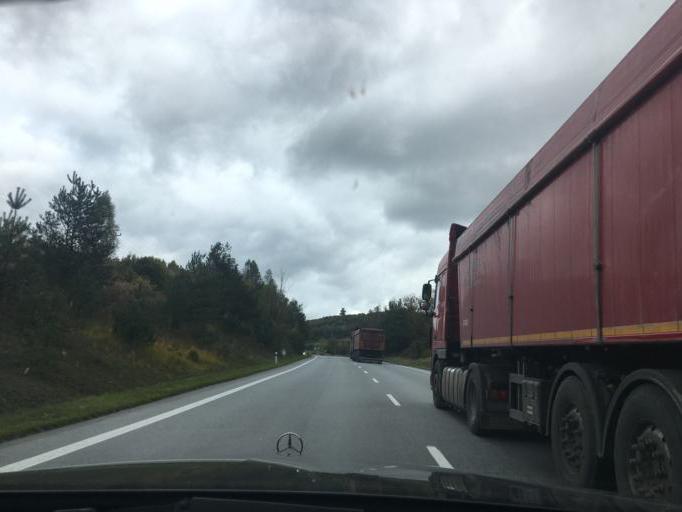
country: PL
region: Subcarpathian Voivodeship
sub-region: Powiat krosnienski
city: Jasliska
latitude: 49.4000
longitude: 21.7026
